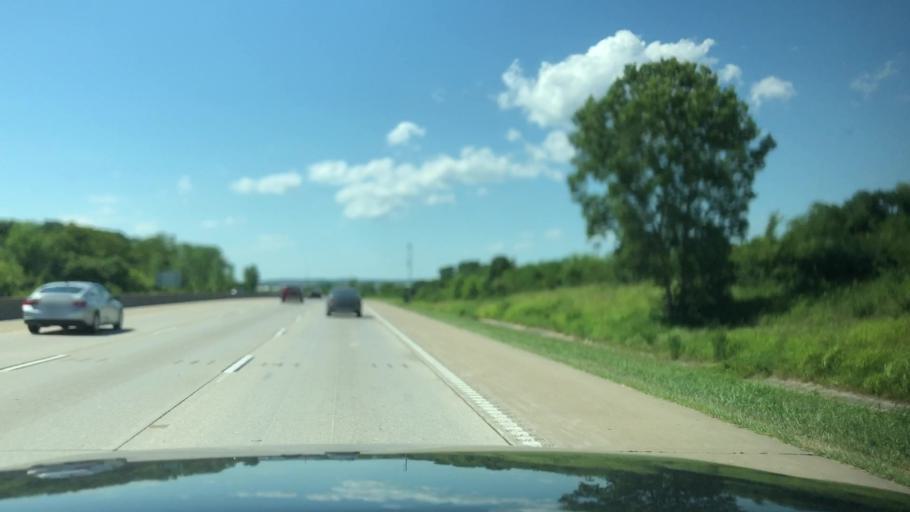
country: US
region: Missouri
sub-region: Saint Charles County
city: Saint Charles
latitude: 38.8152
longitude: -90.4930
